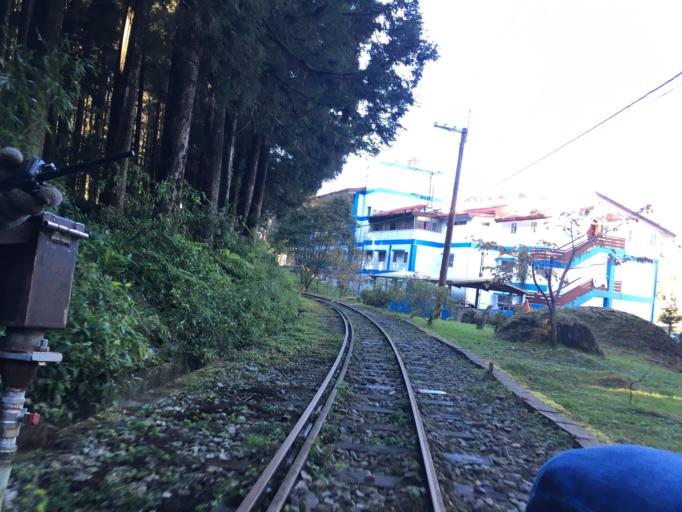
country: TW
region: Taiwan
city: Lugu
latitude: 23.5090
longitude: 120.7914
